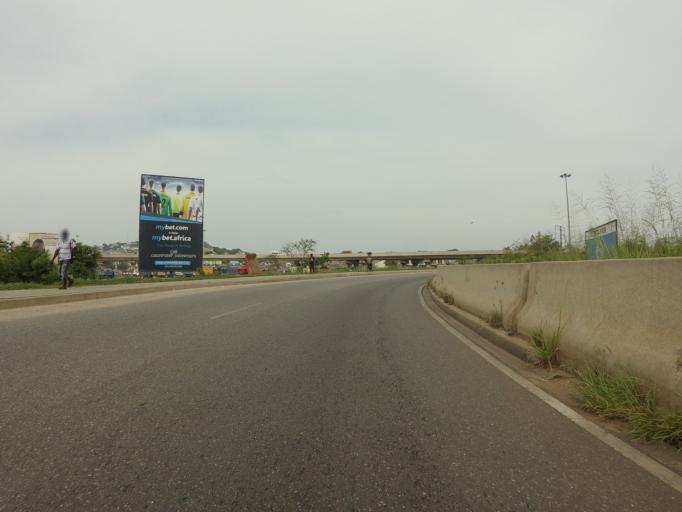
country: GH
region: Greater Accra
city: Gbawe
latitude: 5.5721
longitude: -0.2826
